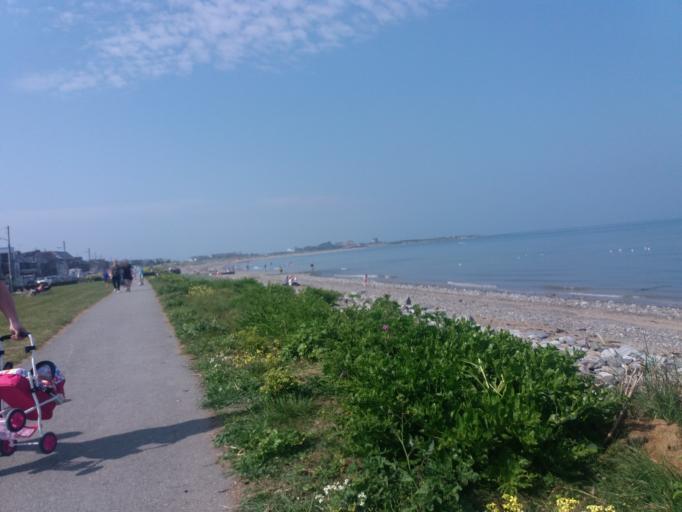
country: IE
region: Leinster
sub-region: Fingal County
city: Skerries
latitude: 53.5751
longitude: -6.1022
